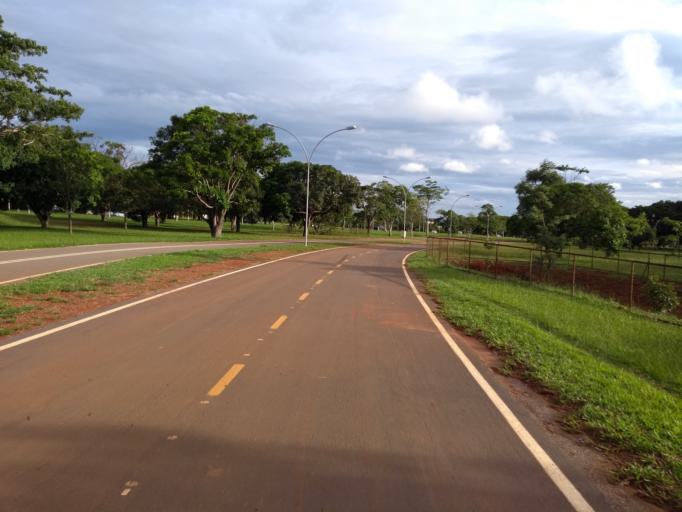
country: BR
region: Federal District
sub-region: Brasilia
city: Brasilia
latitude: -15.8069
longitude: -47.9154
